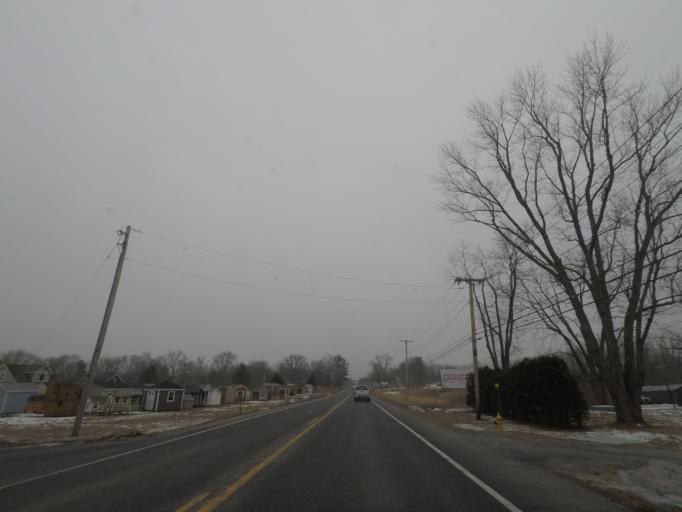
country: US
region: New York
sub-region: Rensselaer County
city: Castleton-on-Hudson
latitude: 42.5514
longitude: -73.8082
